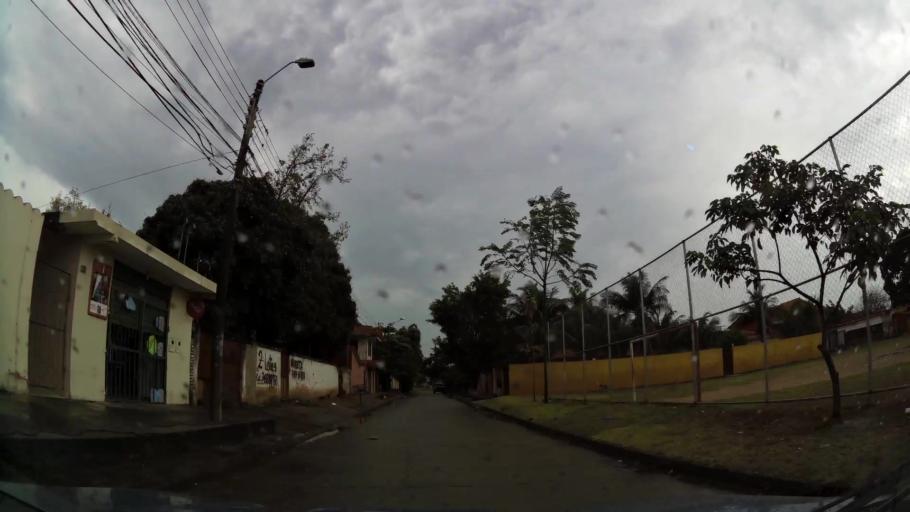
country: BO
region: Santa Cruz
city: Santa Cruz de la Sierra
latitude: -17.7614
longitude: -63.1534
